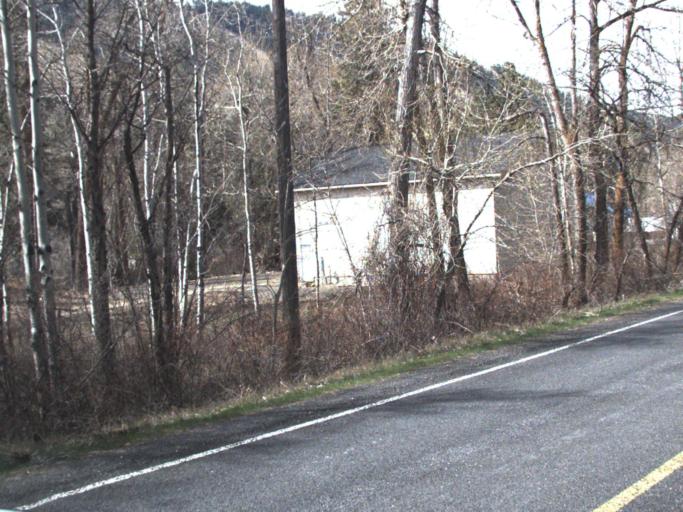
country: US
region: Washington
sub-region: Yakima County
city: Tieton
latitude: 46.7954
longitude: -120.8837
